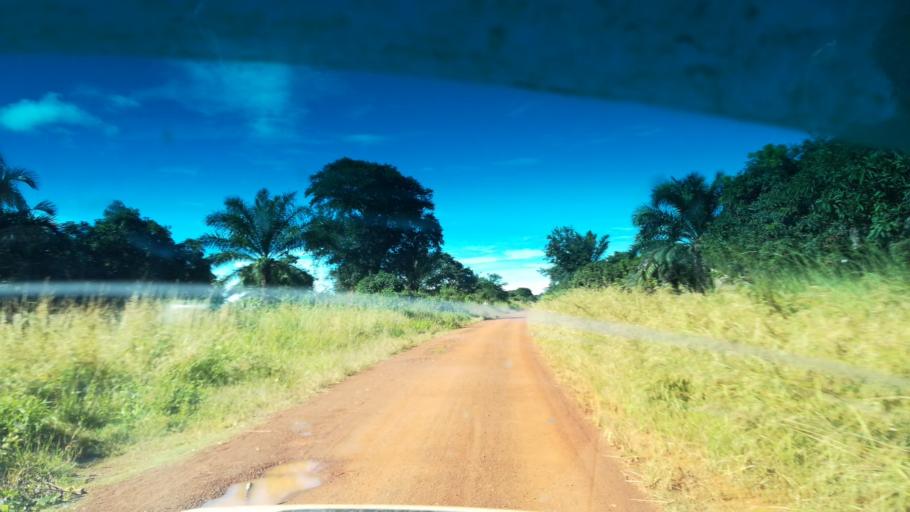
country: ZM
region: Luapula
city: Nchelenge
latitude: -9.3904
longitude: 28.2000
